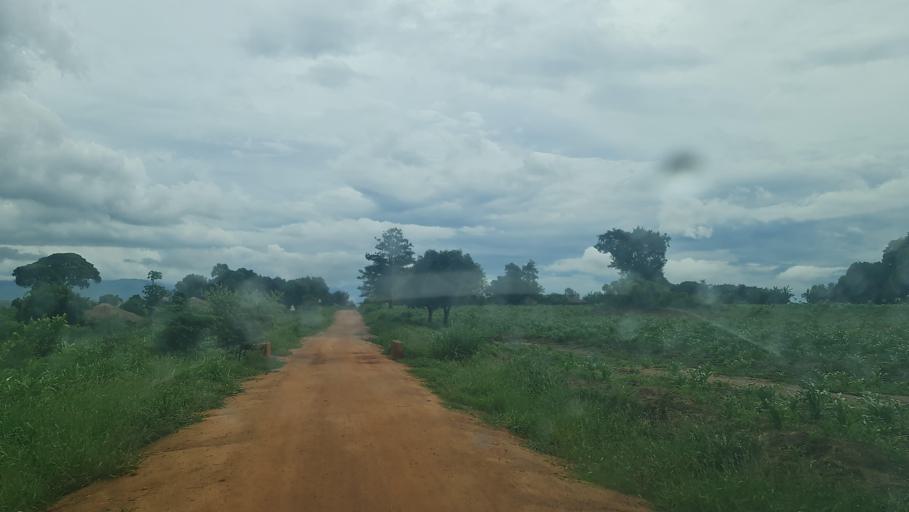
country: MW
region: Southern Region
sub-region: Nsanje District
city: Nsanje
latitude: -17.3955
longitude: 35.5753
